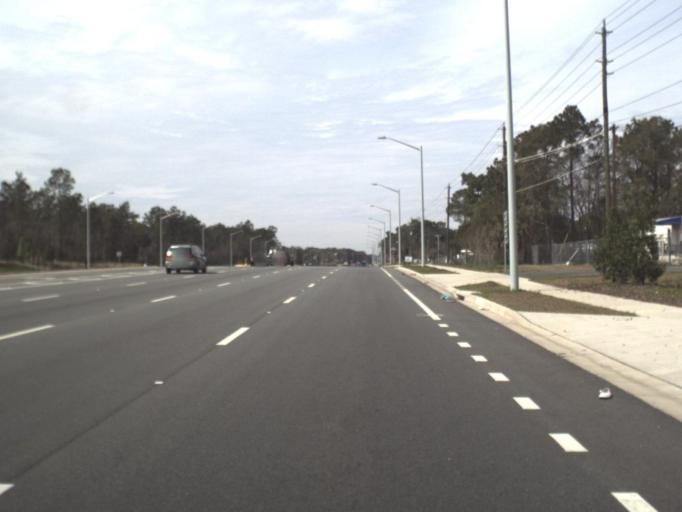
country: US
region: Florida
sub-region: Leon County
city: Tallahassee
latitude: 30.3759
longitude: -84.2804
